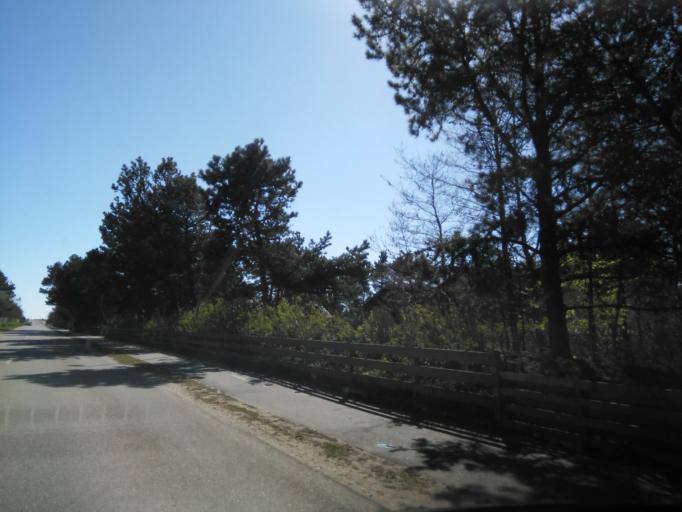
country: DK
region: South Denmark
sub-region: Varde Kommune
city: Oksbol
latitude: 55.5485
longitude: 8.1341
